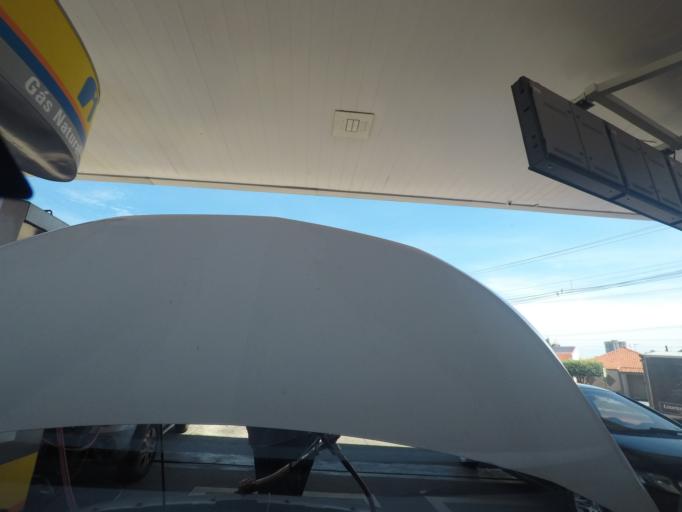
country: BR
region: Sao Paulo
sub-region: Matao
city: Matao
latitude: -21.6152
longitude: -48.3662
